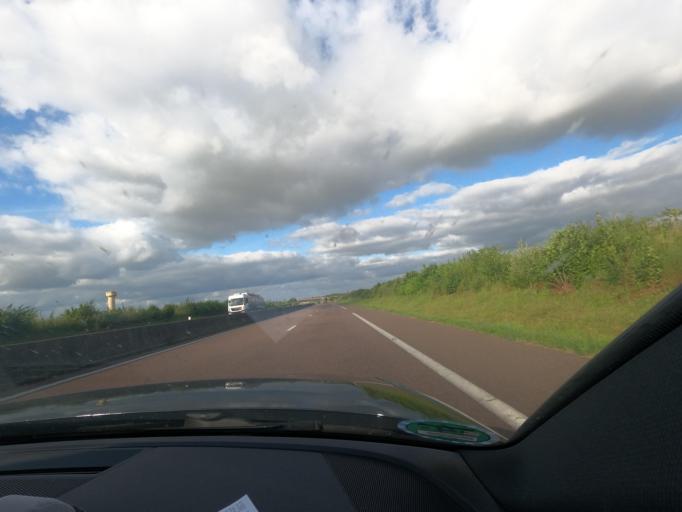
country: FR
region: Picardie
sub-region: Departement de la Somme
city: Poix-de-Picardie
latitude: 49.8141
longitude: 2.0241
